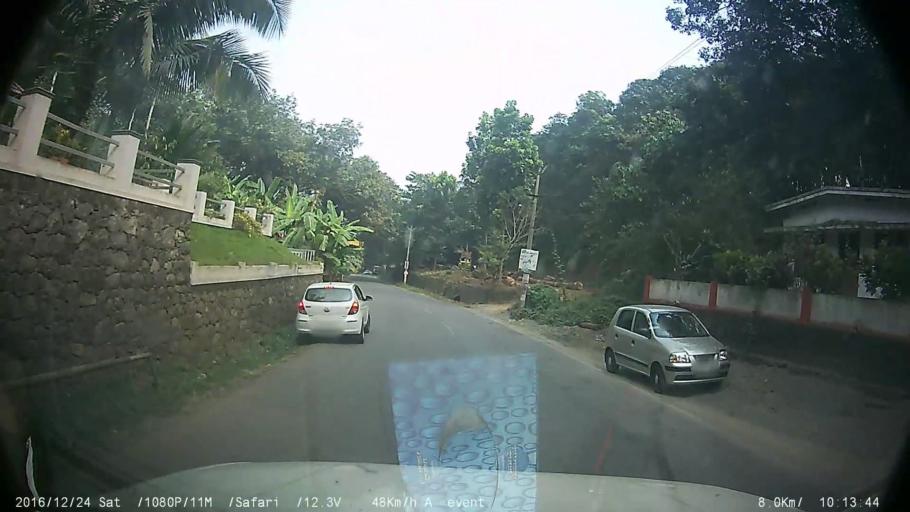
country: IN
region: Kerala
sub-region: Kottayam
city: Palackattumala
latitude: 9.7964
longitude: 76.6125
